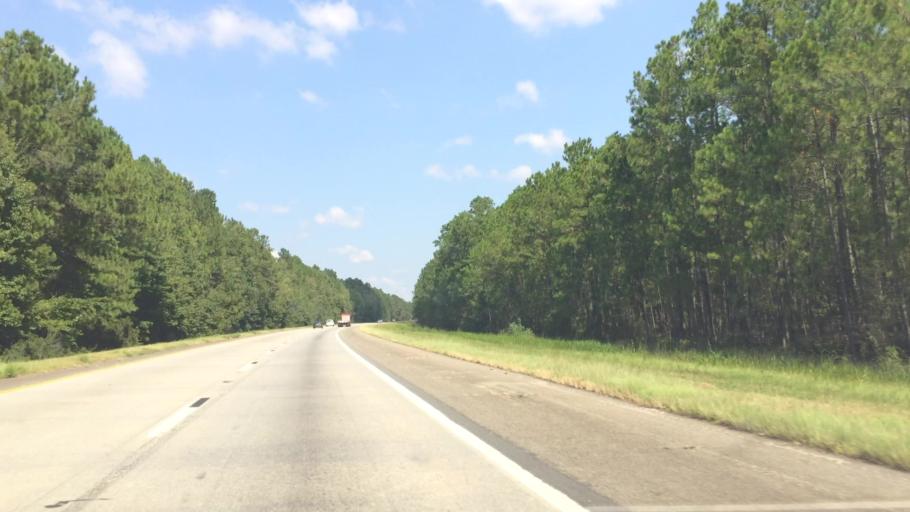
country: US
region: South Carolina
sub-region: Colleton County
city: Walterboro
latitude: 33.0467
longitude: -80.6687
